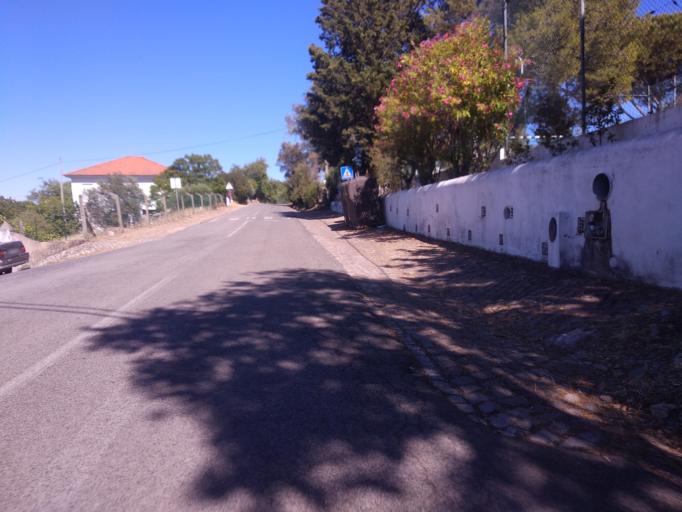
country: PT
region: Faro
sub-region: Sao Bras de Alportel
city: Sao Bras de Alportel
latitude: 37.1706
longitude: -7.8884
